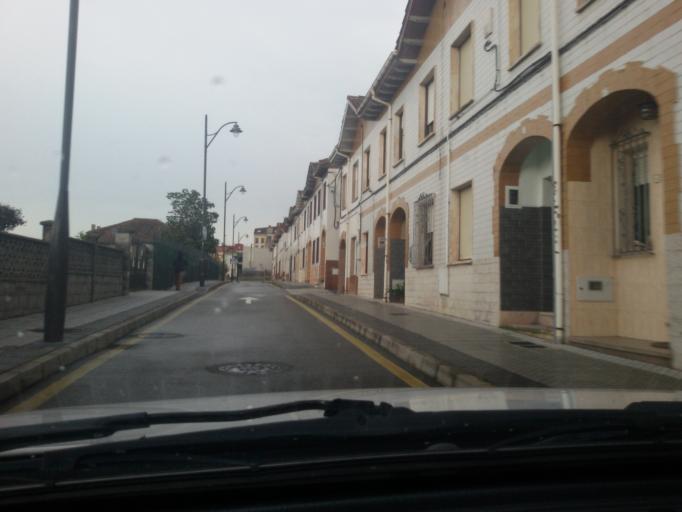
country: ES
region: Asturias
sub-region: Province of Asturias
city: Norena
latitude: 43.3833
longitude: -5.7098
